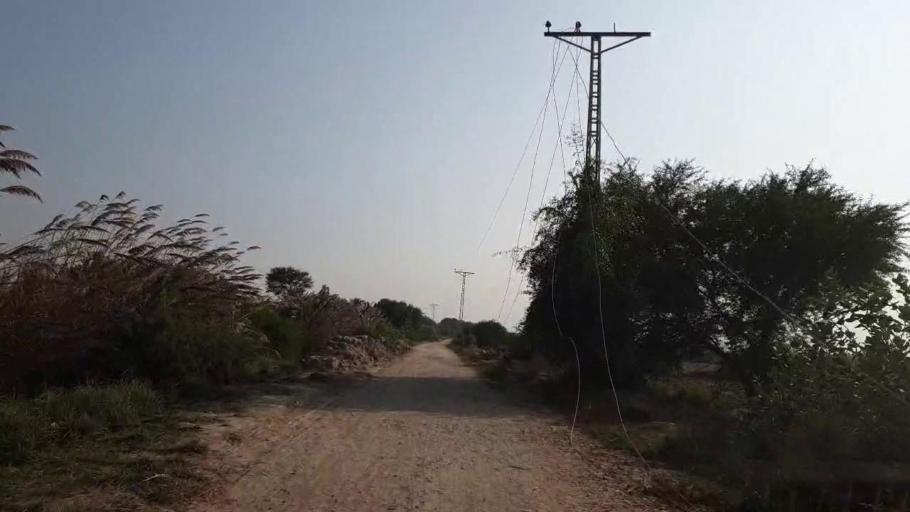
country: PK
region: Sindh
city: Bulri
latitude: 24.9828
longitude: 68.3775
